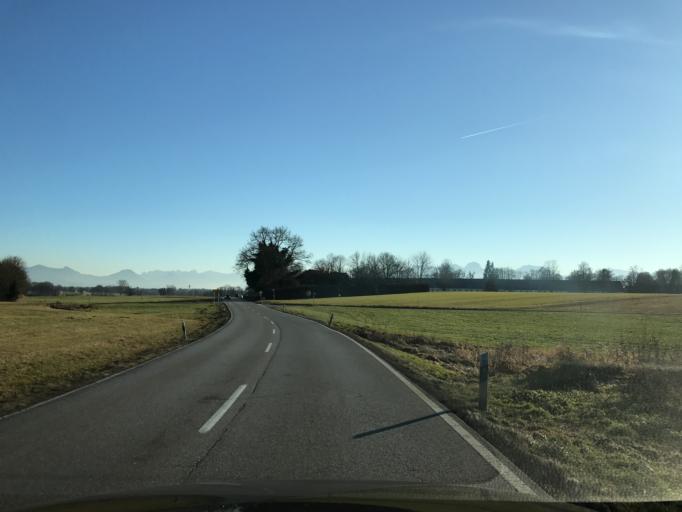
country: DE
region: Bavaria
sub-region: Upper Bavaria
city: Bad Aibling
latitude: 47.8900
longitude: 11.9889
